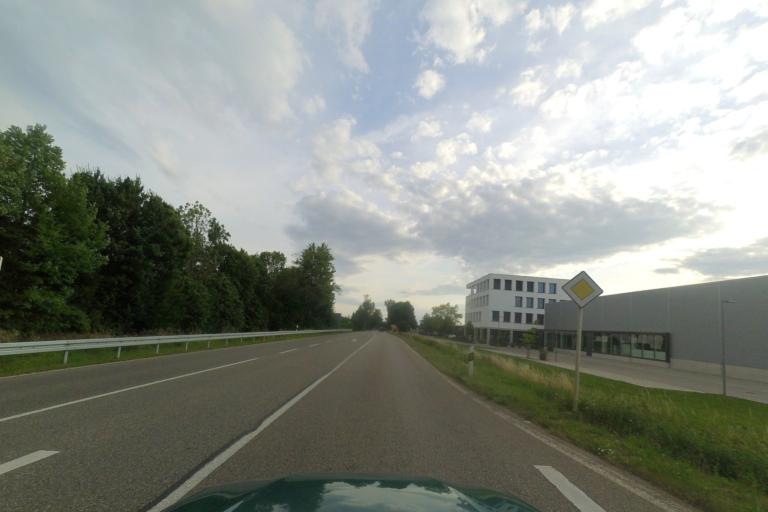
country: DE
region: Bavaria
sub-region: Swabia
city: Hochstadt an der Donau
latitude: 48.6232
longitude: 10.5768
